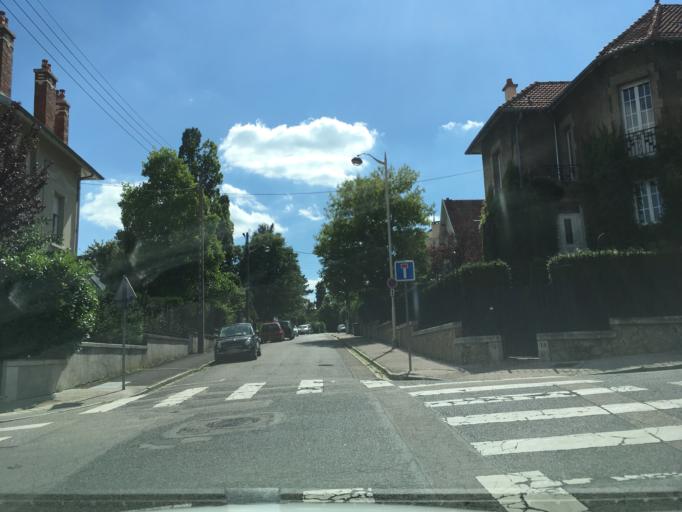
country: FR
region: Lorraine
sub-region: Departement de Meurthe-et-Moselle
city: Laxou
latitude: 48.6899
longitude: 6.1470
